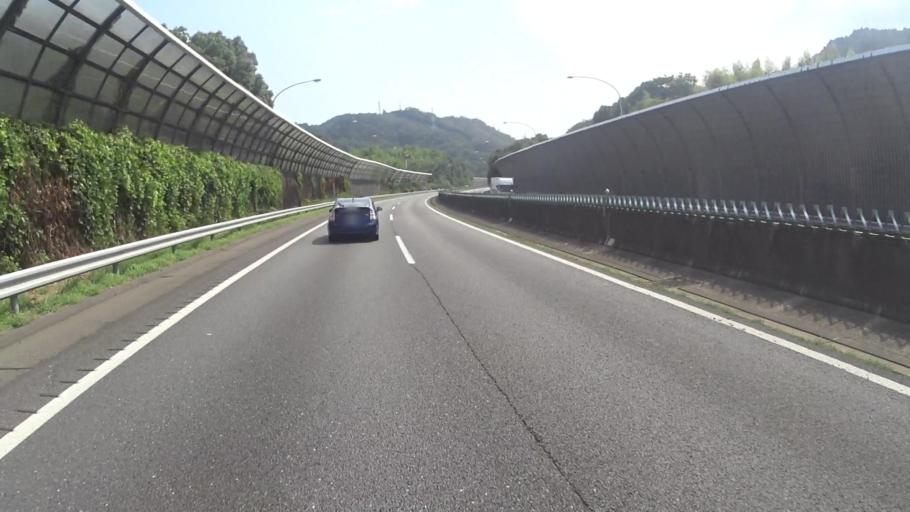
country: JP
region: Shiga Prefecture
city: Otsu-shi
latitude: 34.9874
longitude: 135.8354
